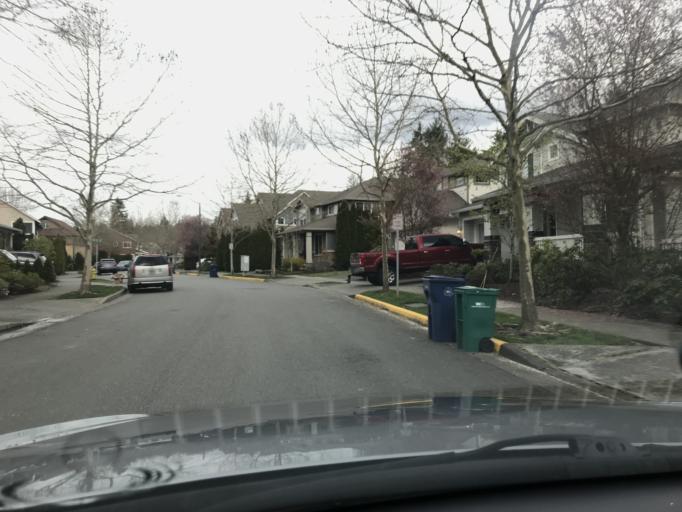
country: US
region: Washington
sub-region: King County
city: Sammamish
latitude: 47.6637
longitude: -122.0829
